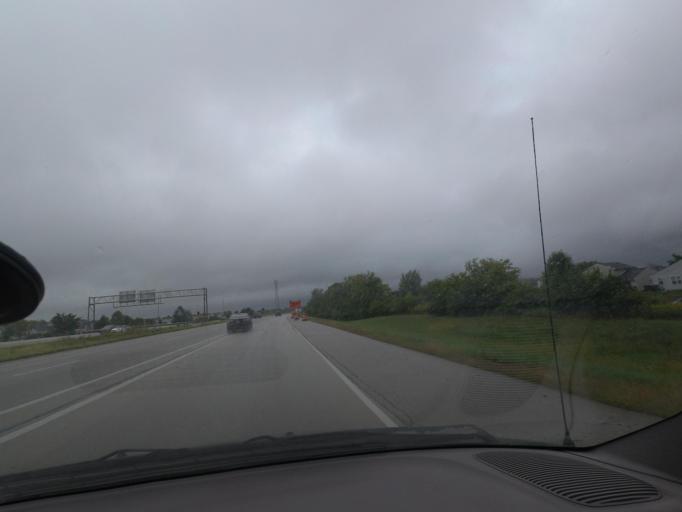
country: US
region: Illinois
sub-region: Champaign County
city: Champaign
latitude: 40.1231
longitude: -88.3049
